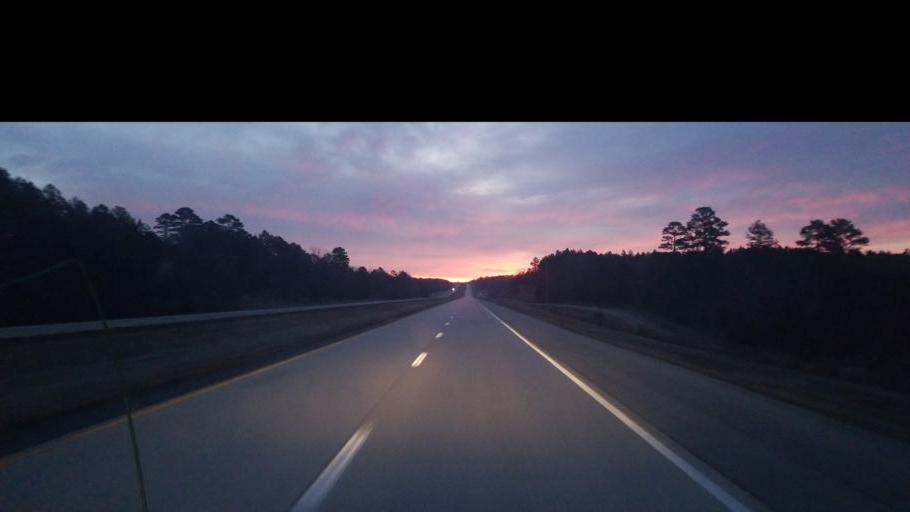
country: US
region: Missouri
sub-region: Shannon County
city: Winona
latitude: 36.9980
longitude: -91.3992
